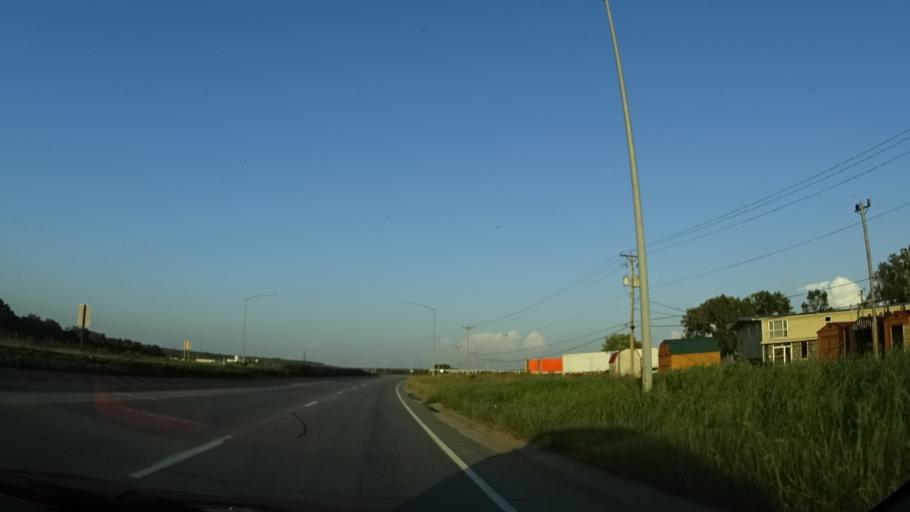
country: US
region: Iowa
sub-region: Pottawattamie County
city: Council Bluffs
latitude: 41.2190
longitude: -95.8780
